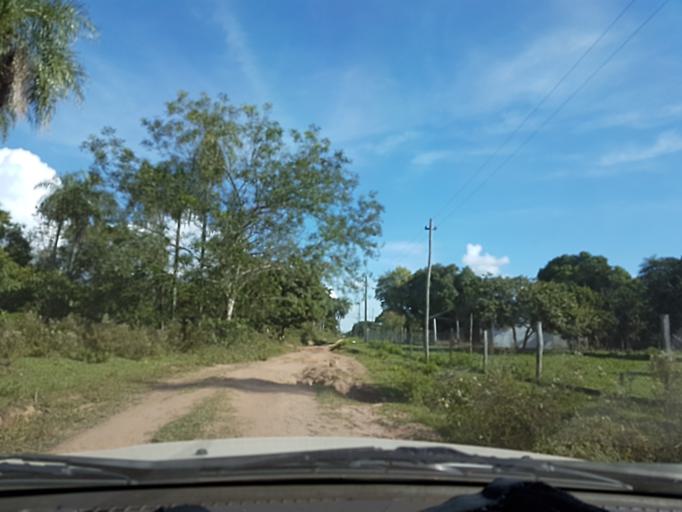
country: PY
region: Cordillera
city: Arroyos y Esteros
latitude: -24.9757
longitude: -57.1943
